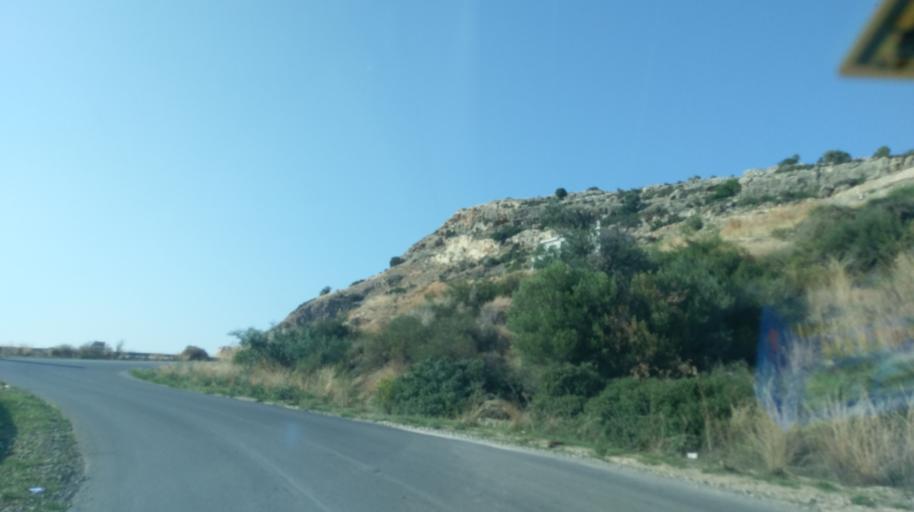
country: CY
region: Lefkosia
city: Kato Pyrgos
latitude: 35.1648
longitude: 32.7517
